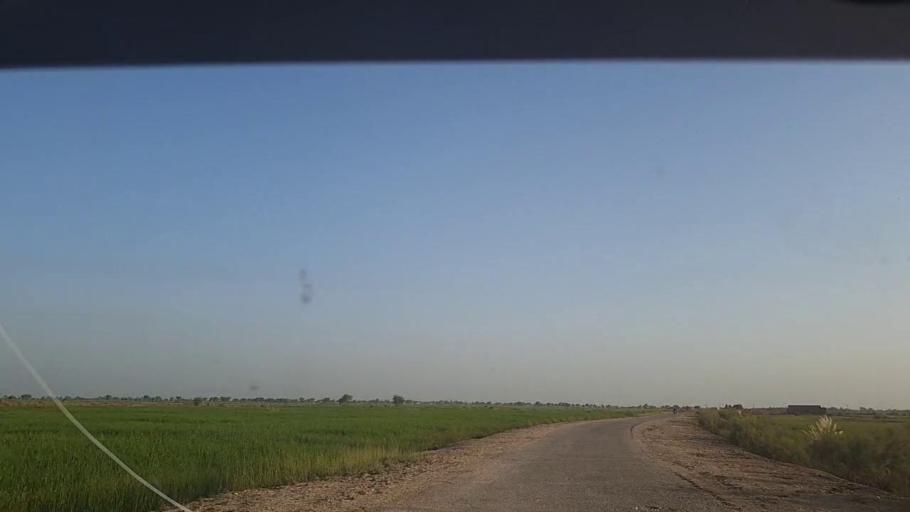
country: PK
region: Sindh
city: Thul
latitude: 28.1455
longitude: 68.8880
